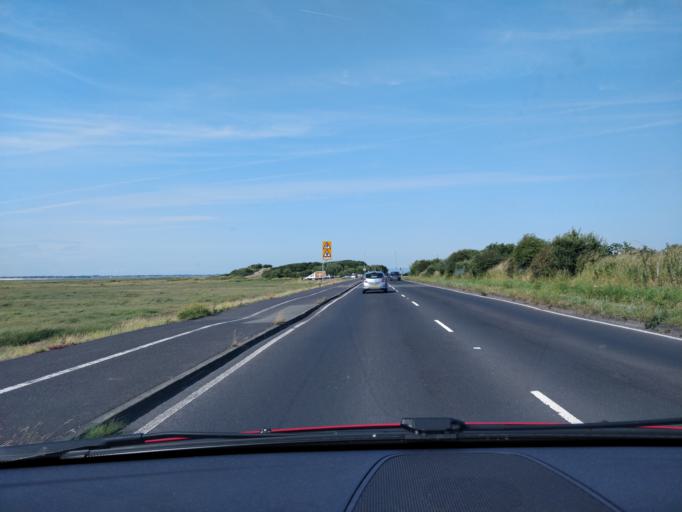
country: GB
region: England
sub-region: Sefton
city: Southport
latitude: 53.6751
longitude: -2.9837
